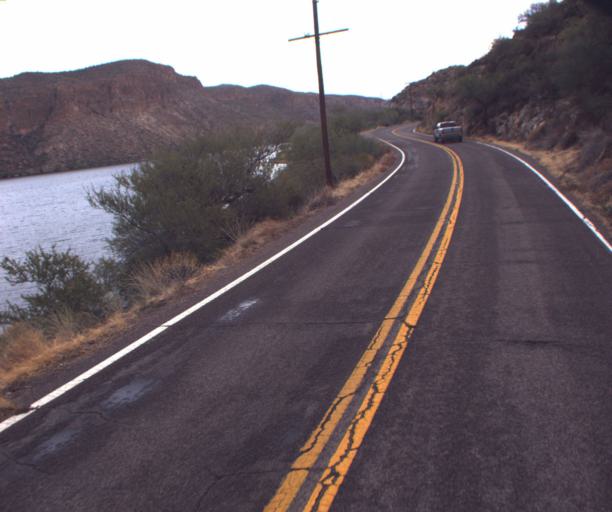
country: US
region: Arizona
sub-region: Pinal County
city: Apache Junction
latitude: 33.5384
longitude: -111.4382
